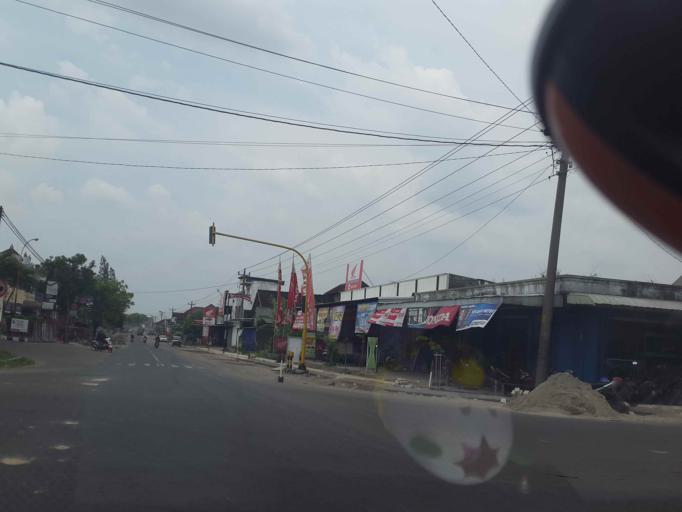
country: ID
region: Central Java
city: Jaten
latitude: -7.6121
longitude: 110.9480
